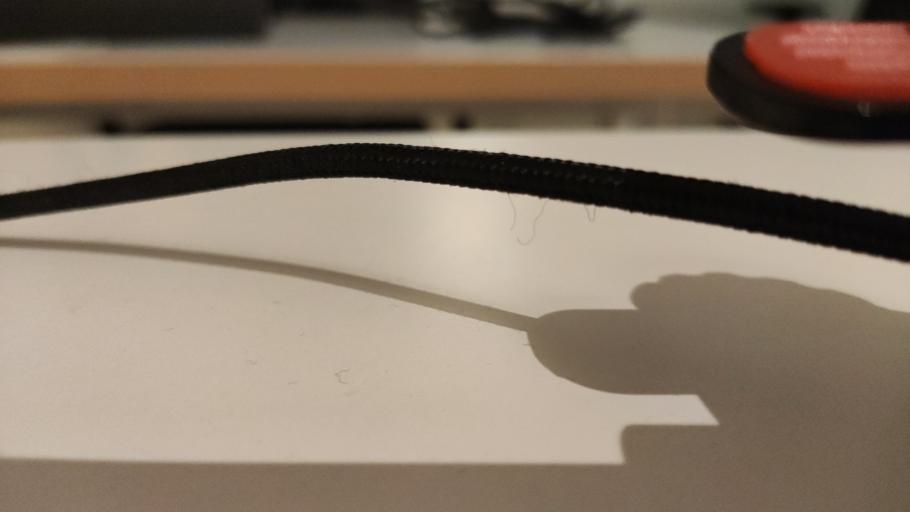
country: RU
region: Moskovskaya
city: Kurovskoye
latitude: 55.5910
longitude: 38.9218
